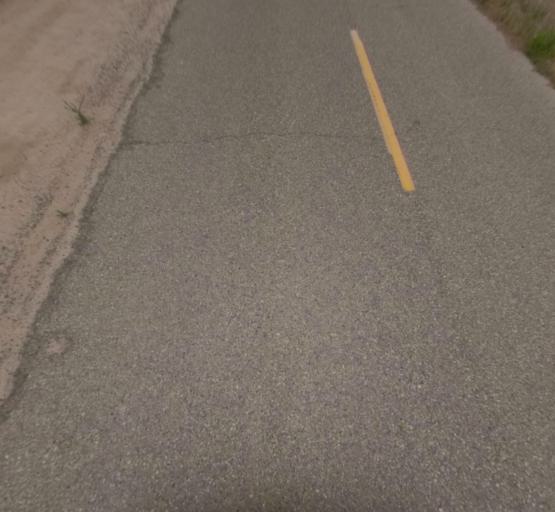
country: US
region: California
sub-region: Madera County
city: Madera
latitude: 36.9326
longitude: -120.1559
